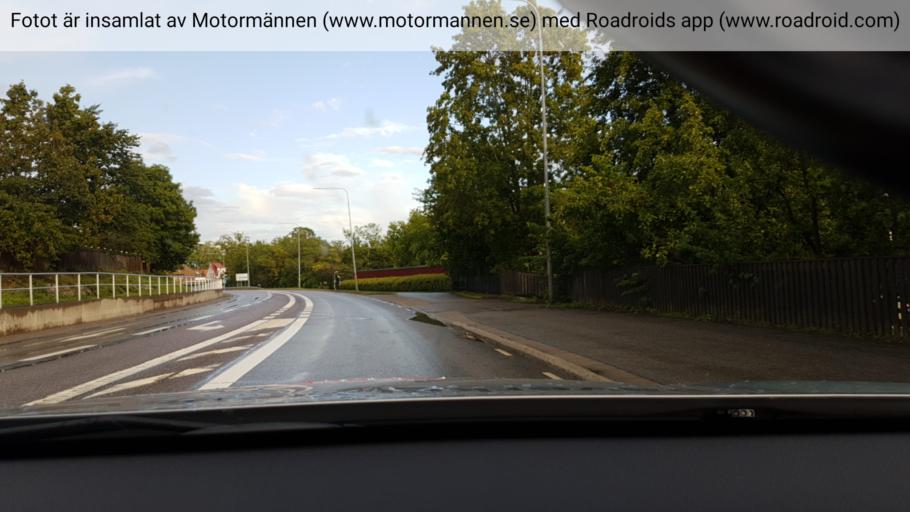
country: SE
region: Stockholm
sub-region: Norrtalje Kommun
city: Norrtalje
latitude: 59.7598
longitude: 18.6913
